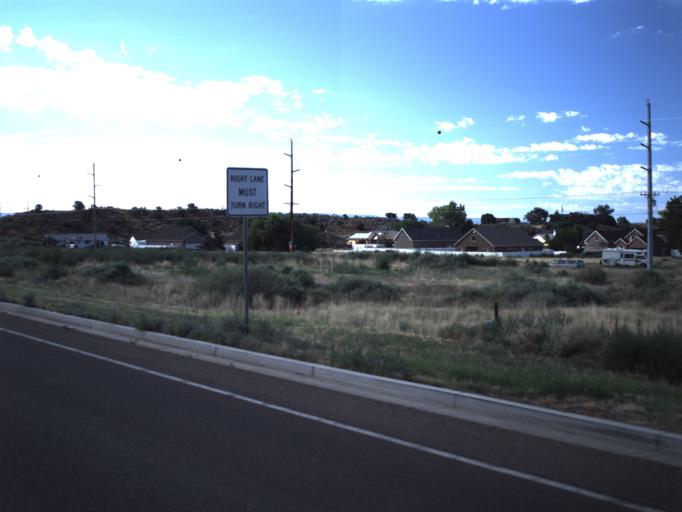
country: US
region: Utah
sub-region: Kane County
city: Kanab
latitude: 37.0413
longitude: -112.5113
